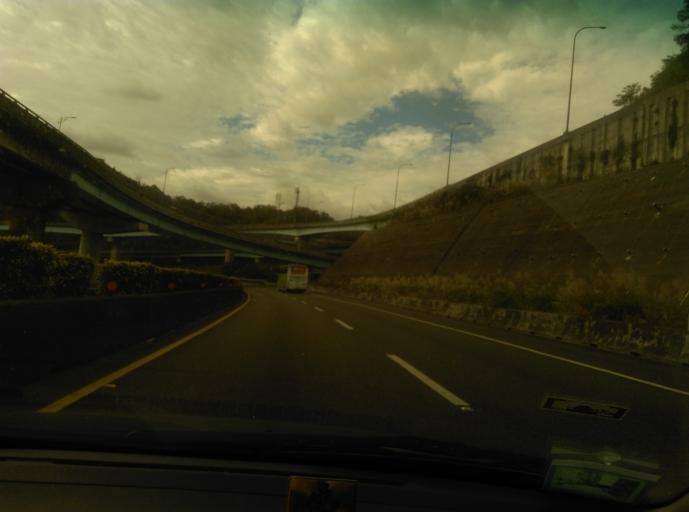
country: TW
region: Taiwan
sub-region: Keelung
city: Keelung
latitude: 25.0976
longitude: 121.7019
